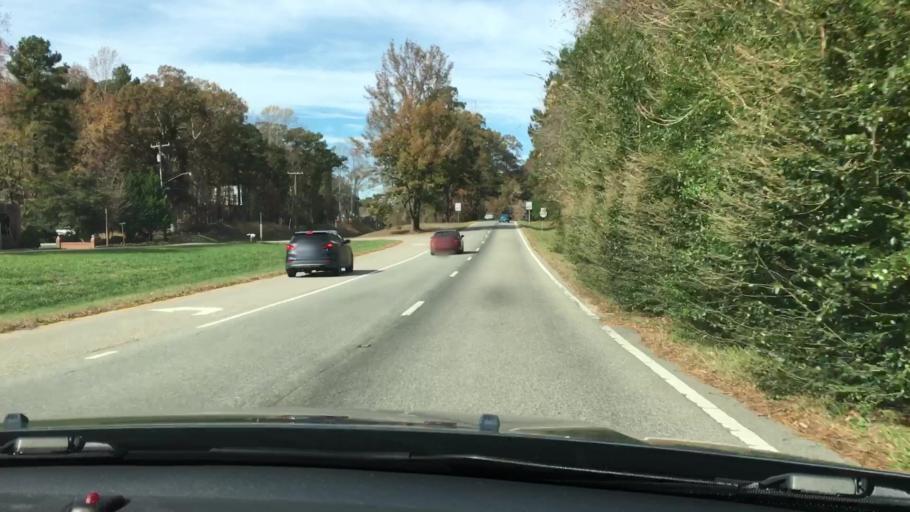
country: US
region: Virginia
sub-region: James City County
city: Williamsburg
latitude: 37.3312
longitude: -76.7438
